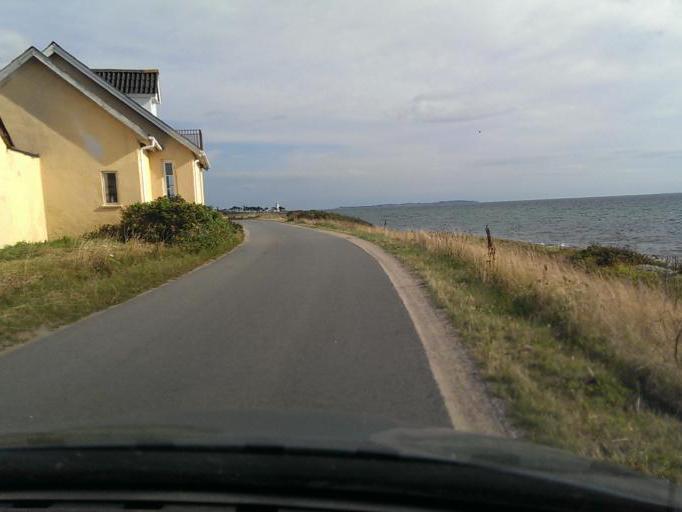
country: DK
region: Central Jutland
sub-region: Syddjurs Kommune
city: Ebeltoft
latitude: 56.1044
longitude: 10.5066
